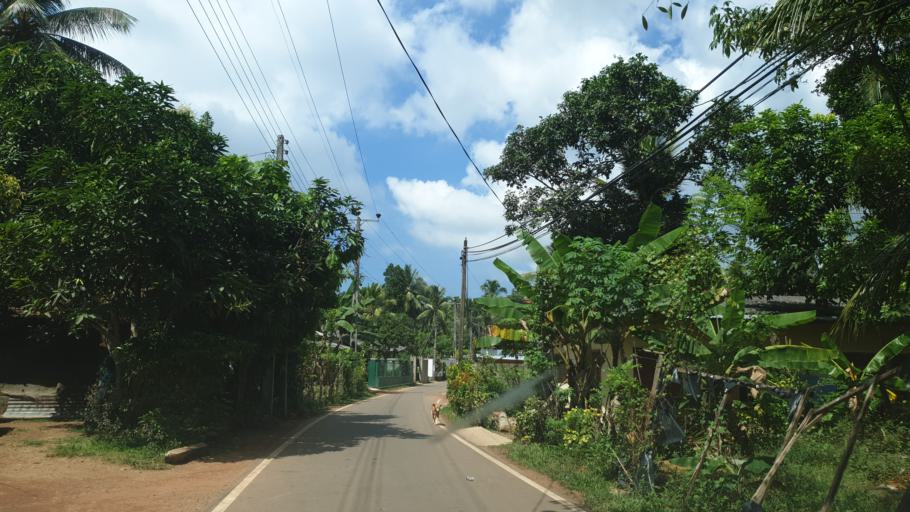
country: LK
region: Western
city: Panadura
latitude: 6.6761
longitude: 79.9718
